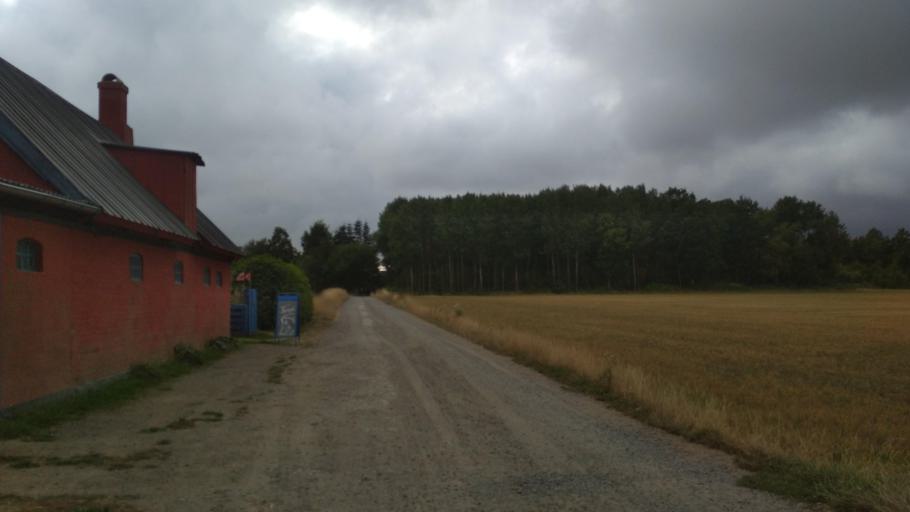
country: DK
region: Capital Region
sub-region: Bornholm Kommune
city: Akirkeby
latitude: 55.0609
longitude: 14.9536
